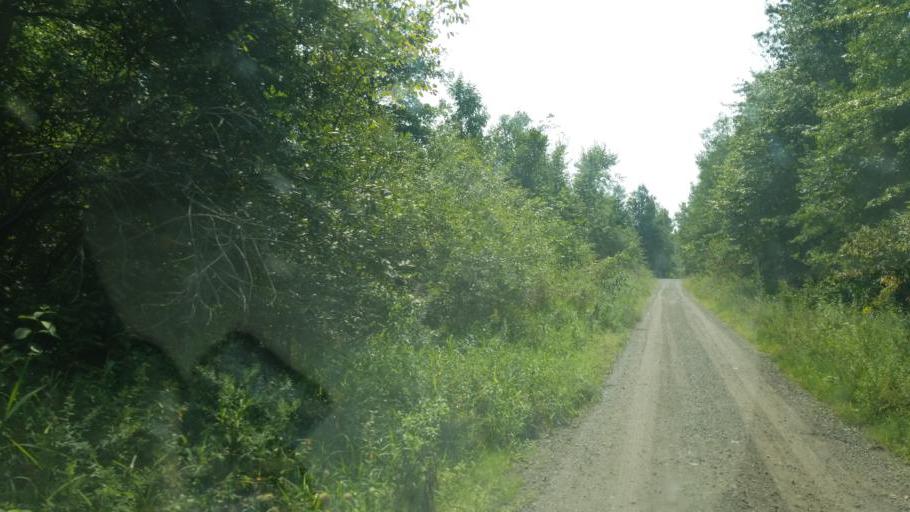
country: US
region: Ohio
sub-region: Ashtabula County
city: Orwell
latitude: 41.4768
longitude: -80.9047
